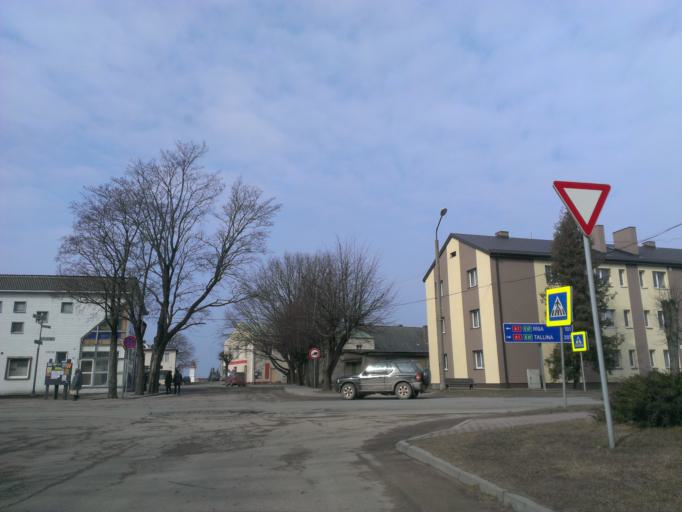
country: LV
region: Salacgrivas
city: Salacgriva
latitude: 57.7557
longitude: 24.3620
